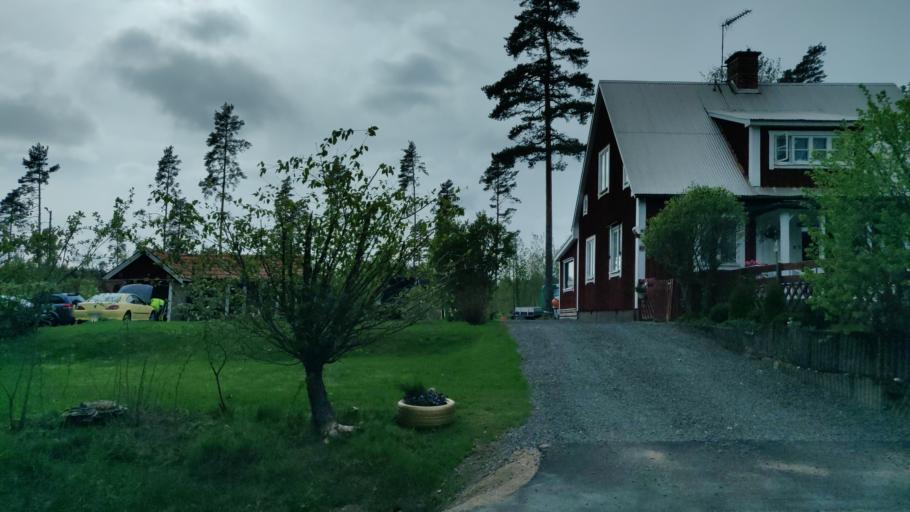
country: SE
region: Vaermland
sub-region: Forshaga Kommun
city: Deje
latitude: 59.6387
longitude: 13.4433
